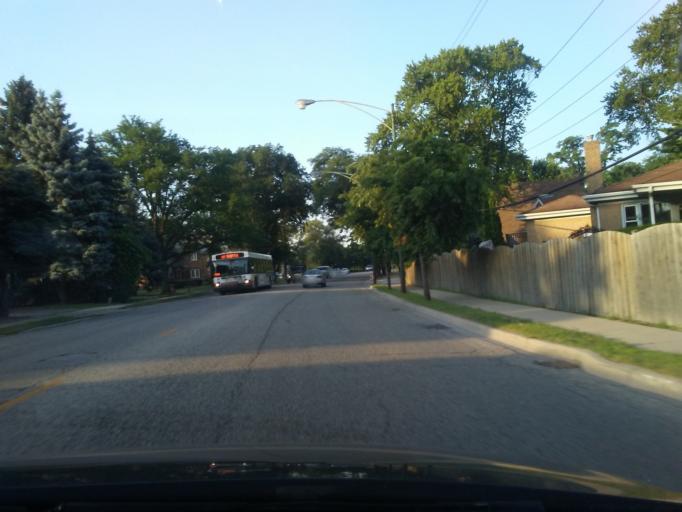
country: US
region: Illinois
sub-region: Cook County
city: Lincolnwood
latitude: 42.0031
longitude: -87.7619
